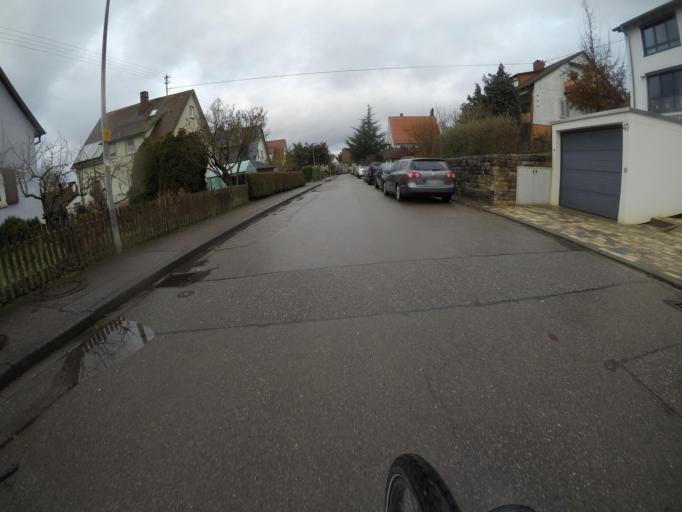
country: DE
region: Baden-Wuerttemberg
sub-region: Regierungsbezirk Stuttgart
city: Vaihingen an der Enz
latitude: 48.9333
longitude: 8.9648
